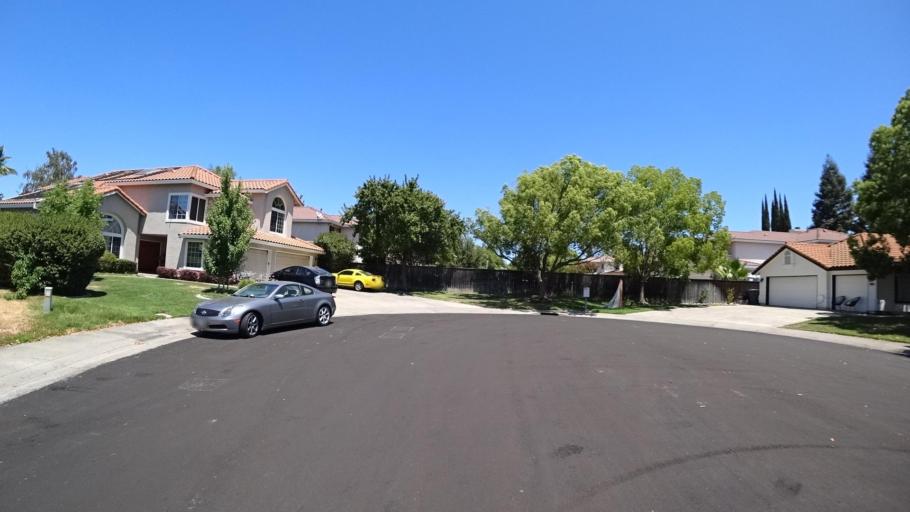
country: US
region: California
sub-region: Placer County
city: Rocklin
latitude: 38.8210
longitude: -121.2571
